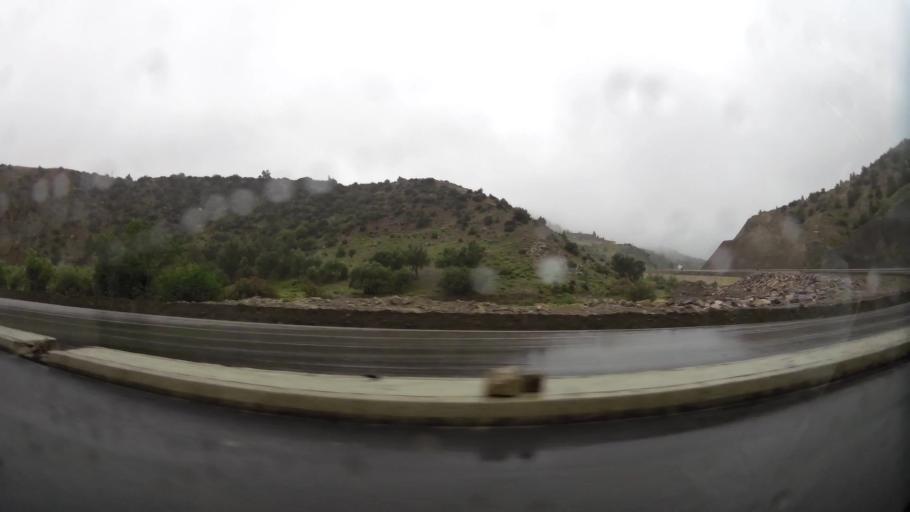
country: MA
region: Taza-Al Hoceima-Taounate
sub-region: Taza
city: Aknoul
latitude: 34.7903
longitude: -3.7567
